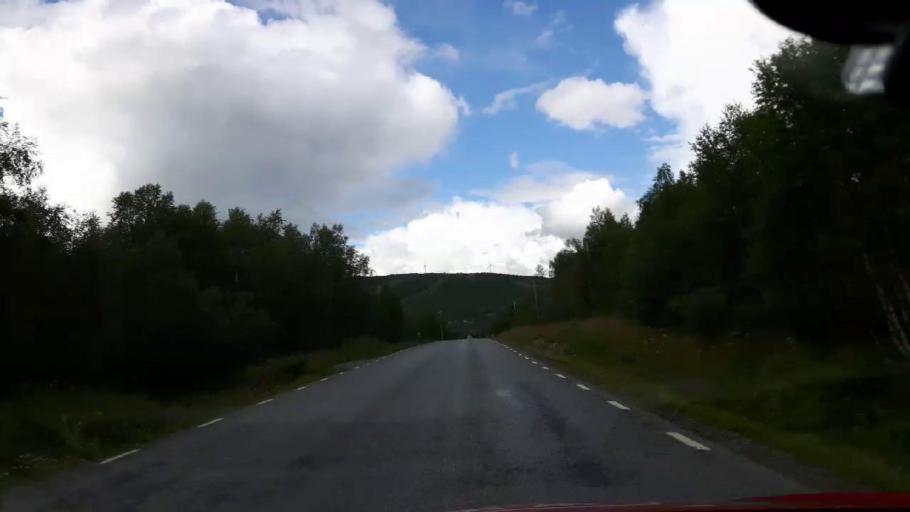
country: NO
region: Nordland
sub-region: Hattfjelldal
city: Hattfjelldal
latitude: 65.0645
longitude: 14.8298
